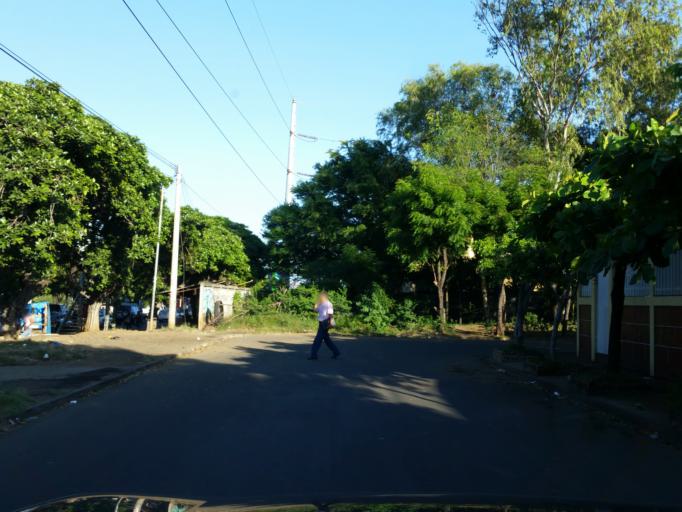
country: NI
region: Managua
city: Managua
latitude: 12.1254
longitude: -86.2848
